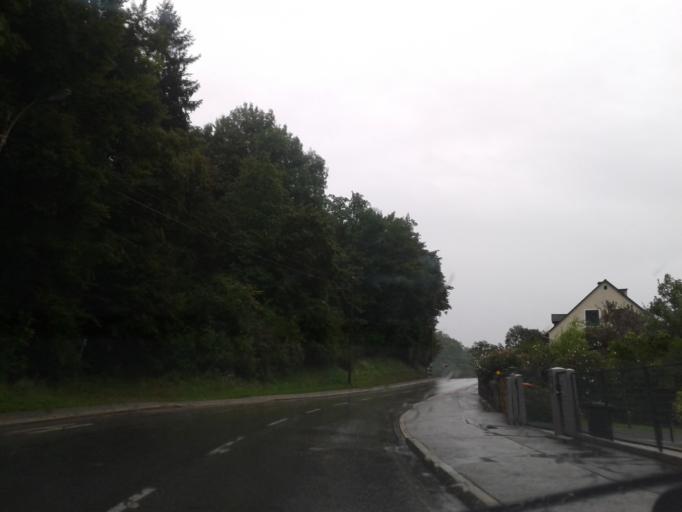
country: AT
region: Styria
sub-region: Graz Stadt
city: Goesting
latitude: 47.1002
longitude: 15.3804
